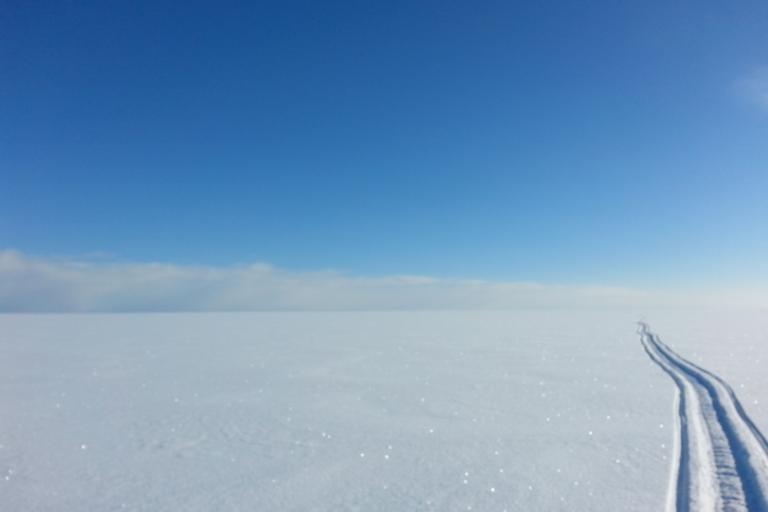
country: RU
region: Leningrad
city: Roshchino
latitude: 60.1578
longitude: 29.6028
